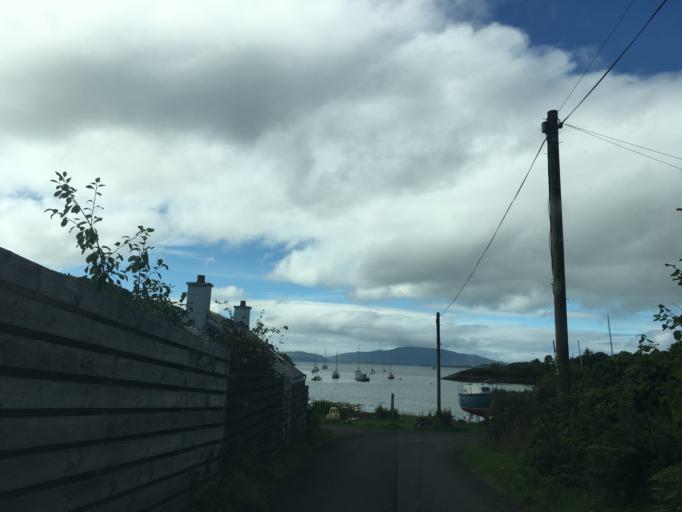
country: GB
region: Scotland
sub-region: Argyll and Bute
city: Ardrishaig
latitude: 56.0875
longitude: -5.5653
